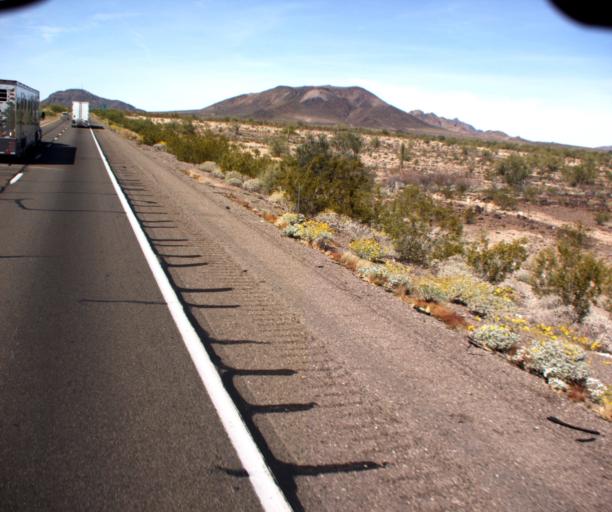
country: US
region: Arizona
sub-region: La Paz County
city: Quartzsite
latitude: 33.6596
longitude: -113.9904
